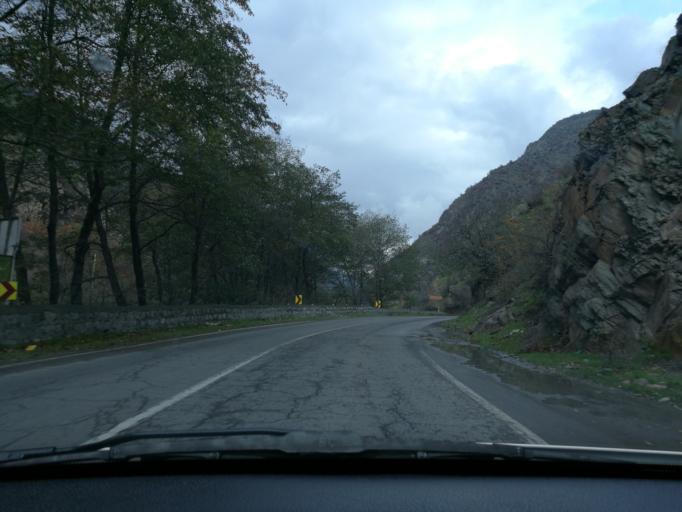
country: IR
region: Mazandaran
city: Chalus
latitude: 36.3354
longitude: 51.2573
